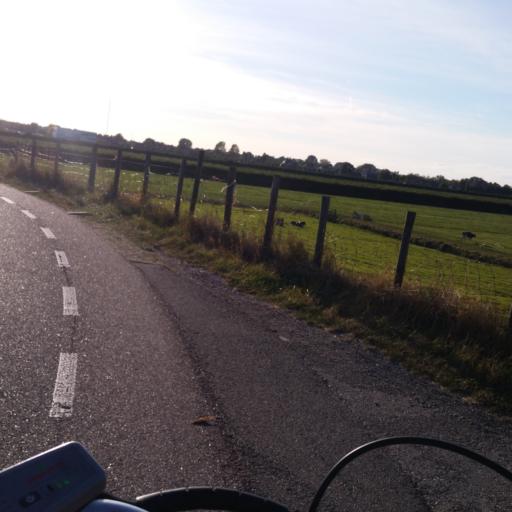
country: NL
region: Utrecht
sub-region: Gemeente Lopik
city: Lopik
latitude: 51.9769
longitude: 4.9851
